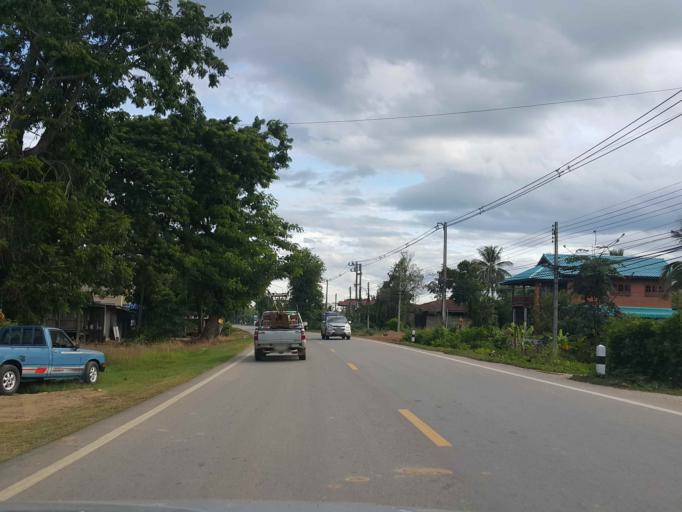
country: TH
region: Sukhothai
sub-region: Amphoe Si Satchanalai
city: Si Satchanalai
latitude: 17.5084
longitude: 99.7534
